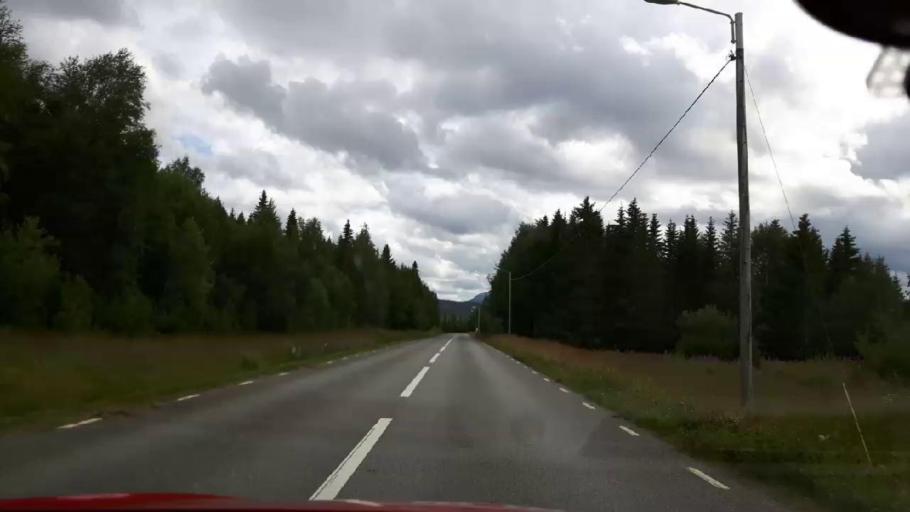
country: NO
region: Nord-Trondelag
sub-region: Lierne
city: Sandvika
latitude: 64.3934
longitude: 14.3685
